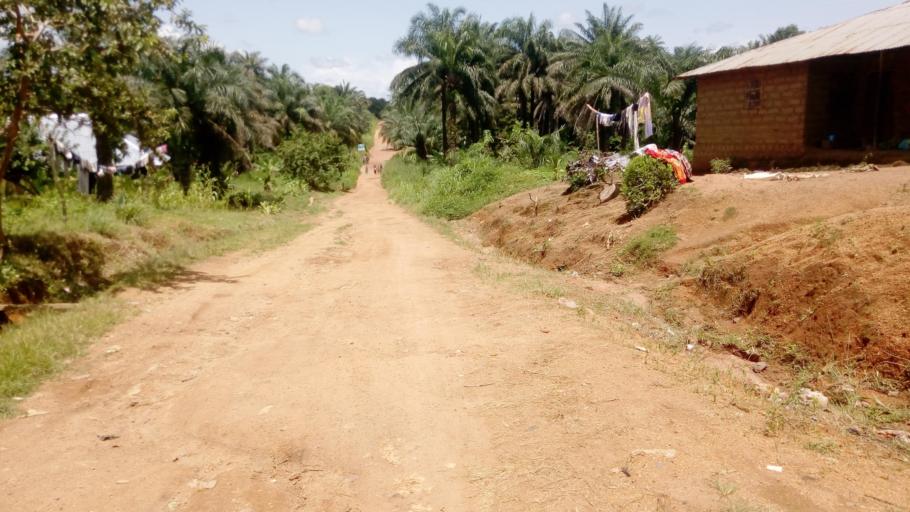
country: SL
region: Northern Province
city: Binkolo
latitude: 8.9567
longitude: -11.9644
